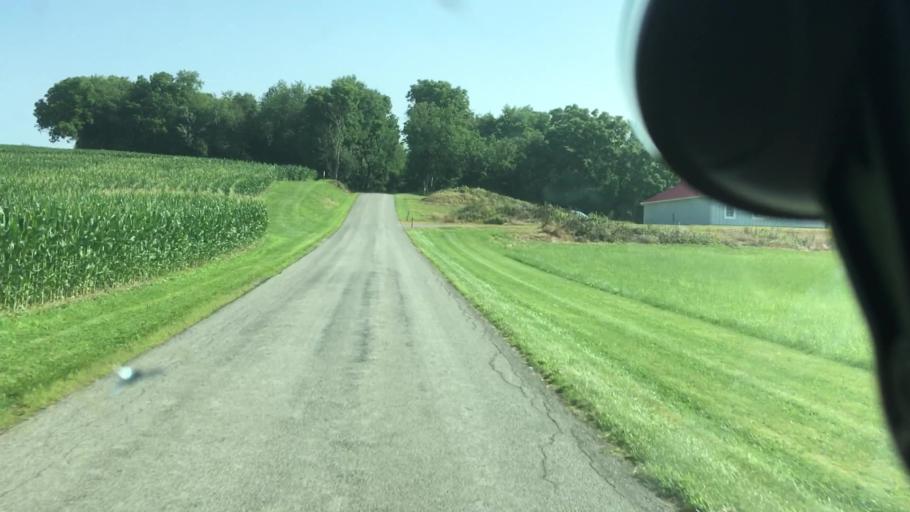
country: US
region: Pennsylvania
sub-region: Butler County
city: Slippery Rock
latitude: 41.0520
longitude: -80.1735
